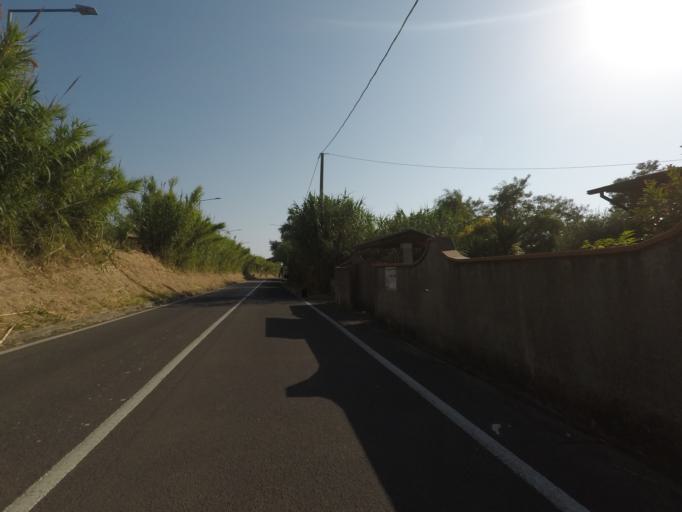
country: IT
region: Liguria
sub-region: Provincia di La Spezia
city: Casano-Dogana-Isola
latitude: 44.0614
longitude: 10.0300
